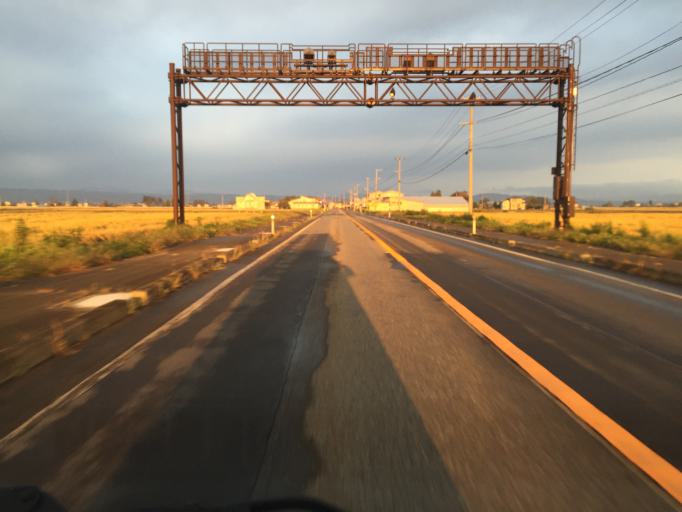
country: JP
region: Fukushima
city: Kitakata
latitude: 37.5533
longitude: 139.8808
